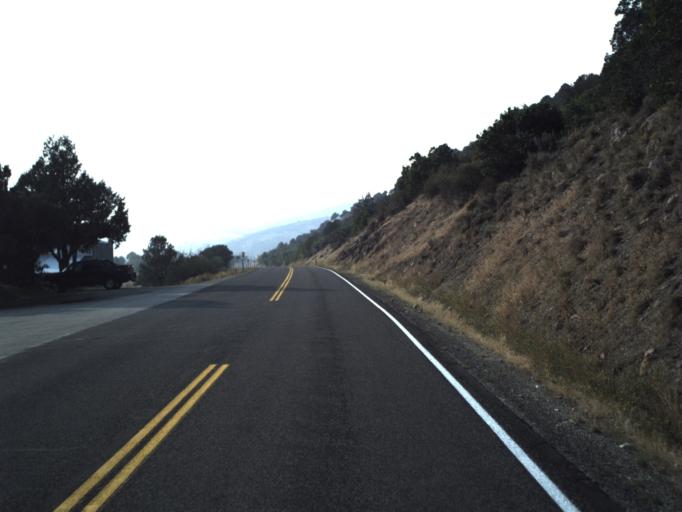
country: US
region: Utah
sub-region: Summit County
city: Francis
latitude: 40.6179
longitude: -111.2140
